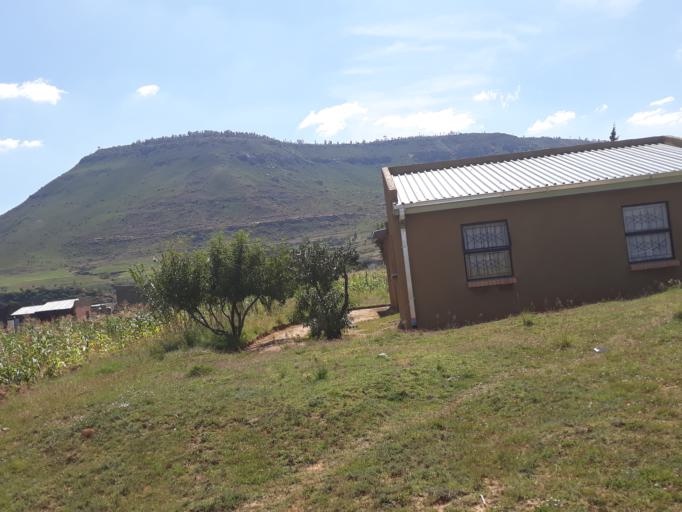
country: LS
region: Mohale's Hoek District
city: Mohale's Hoek
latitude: -30.1022
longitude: 27.4712
